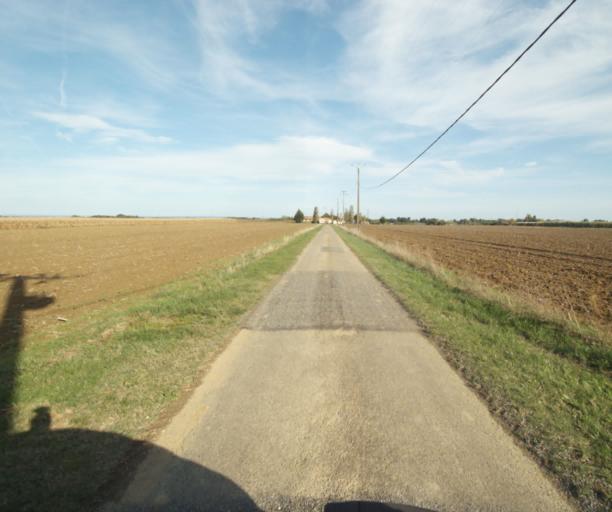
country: FR
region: Midi-Pyrenees
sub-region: Departement du Tarn-et-Garonne
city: Finhan
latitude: 43.9205
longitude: 1.1310
